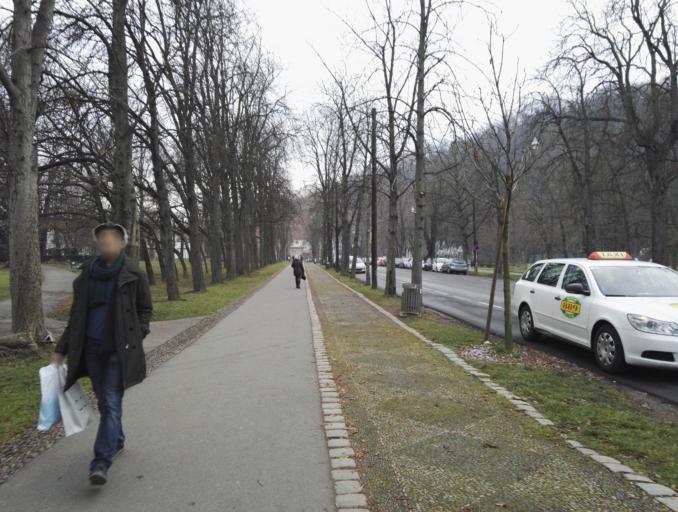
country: AT
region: Styria
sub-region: Graz Stadt
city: Graz
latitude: 47.0775
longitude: 15.4432
